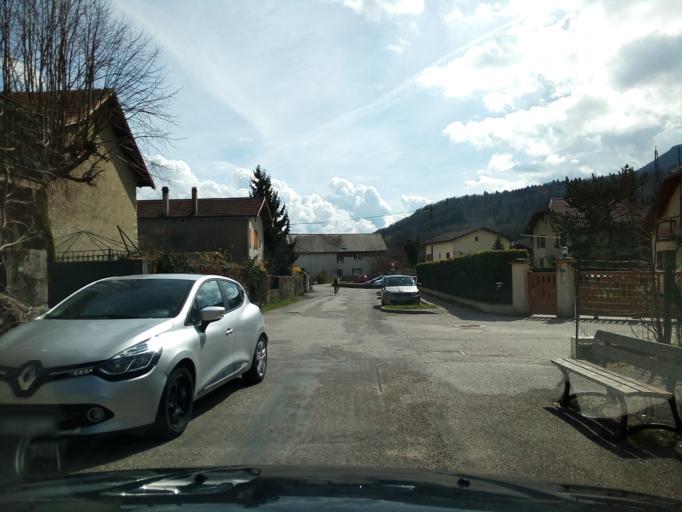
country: FR
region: Rhone-Alpes
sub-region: Departement de l'Isere
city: Chapareillan
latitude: 45.4718
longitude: 5.9865
